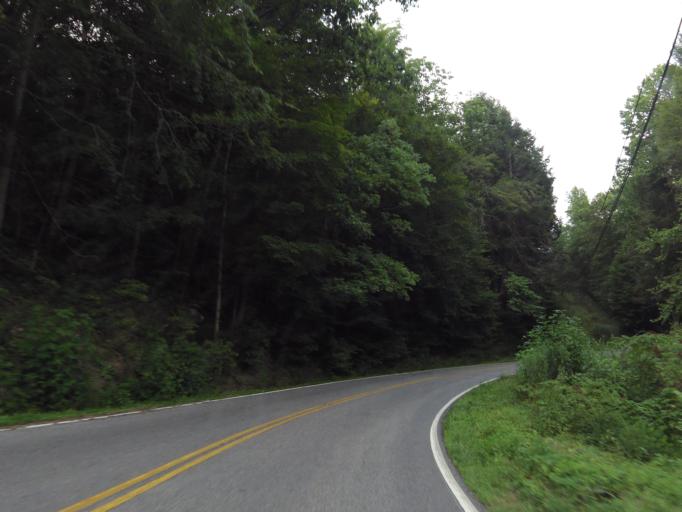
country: US
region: Tennessee
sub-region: Anderson County
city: Clinton
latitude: 36.1344
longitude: -84.2177
